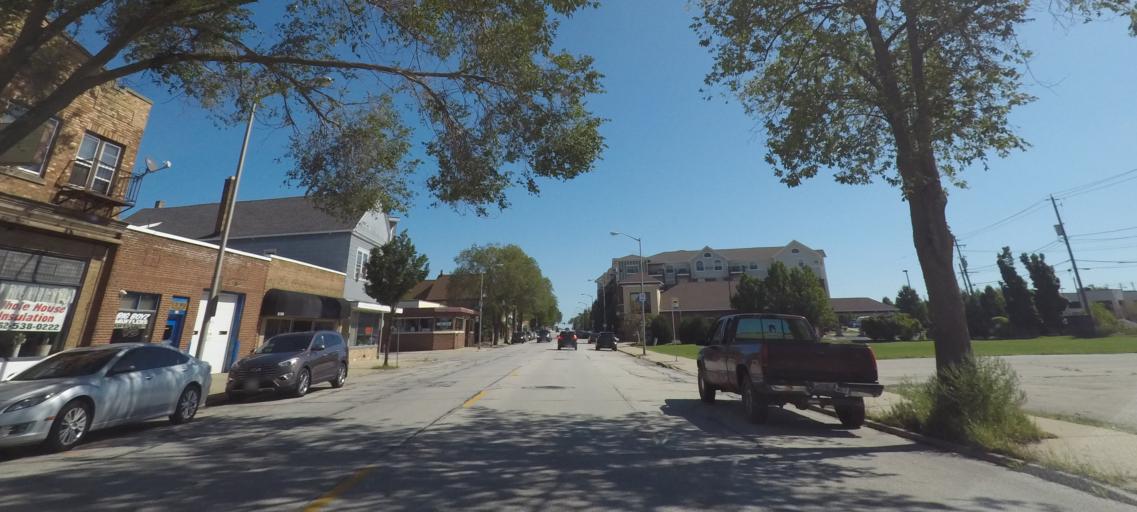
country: US
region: Wisconsin
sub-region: Milwaukee County
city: West Allis
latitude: 43.0106
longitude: -88.0137
